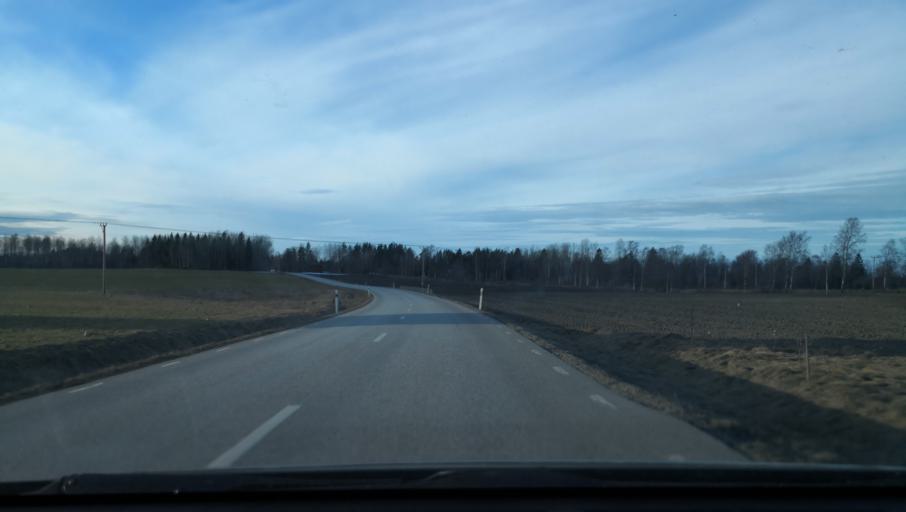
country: SE
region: Uppsala
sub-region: Osthammars Kommun
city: OEsthammar
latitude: 60.3214
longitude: 18.2561
